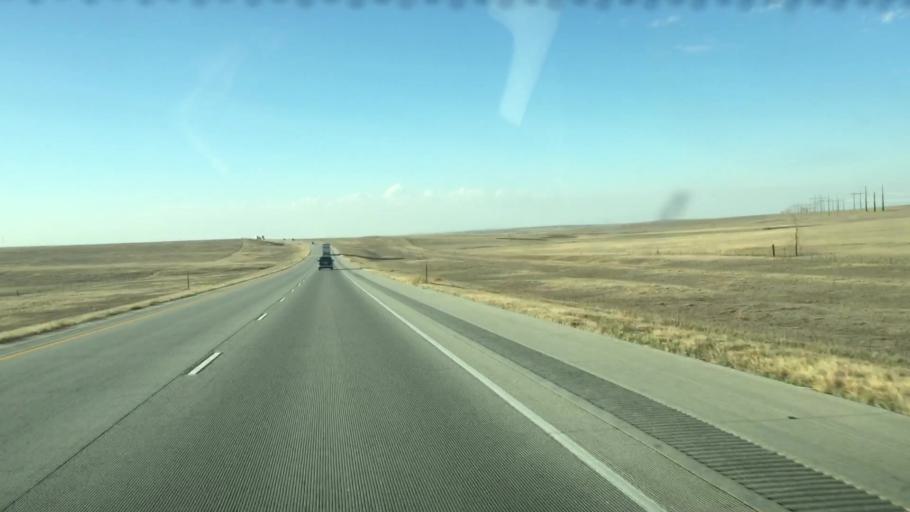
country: US
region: Colorado
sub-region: Lincoln County
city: Limon
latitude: 39.4085
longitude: -103.8986
